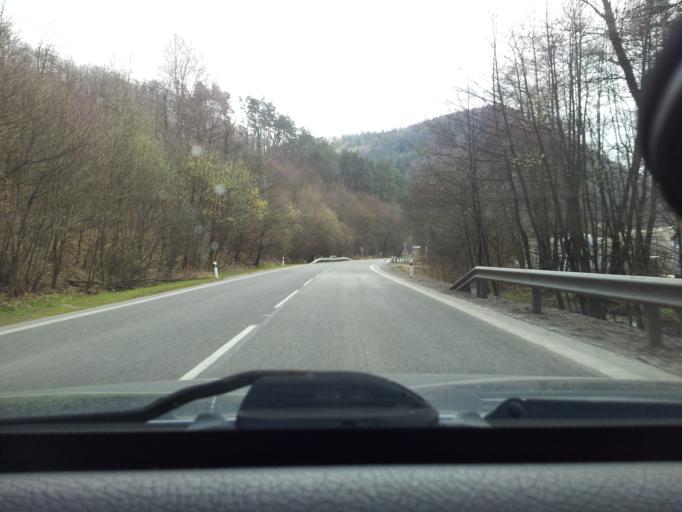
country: SK
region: Banskobystricky
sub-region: Okres Ziar nad Hronom
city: Kremnica
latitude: 48.6839
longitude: 18.9189
